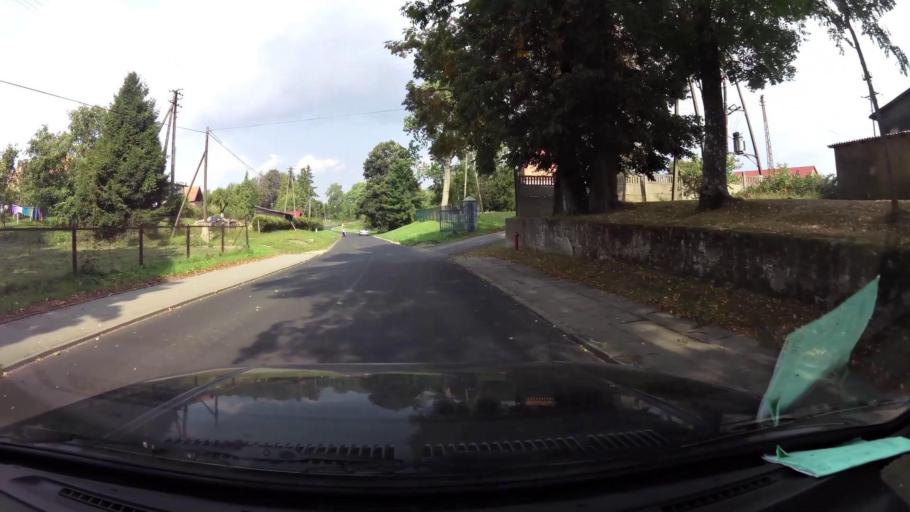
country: PL
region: Pomeranian Voivodeship
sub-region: Powiat slupski
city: Kepice
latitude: 54.1663
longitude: 16.8208
